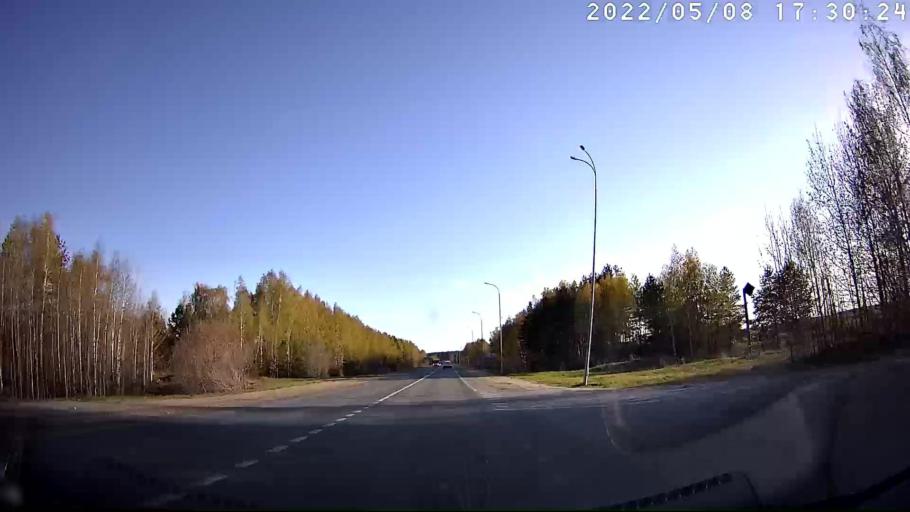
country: RU
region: Mariy-El
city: Volzhsk
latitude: 55.9106
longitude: 48.3637
